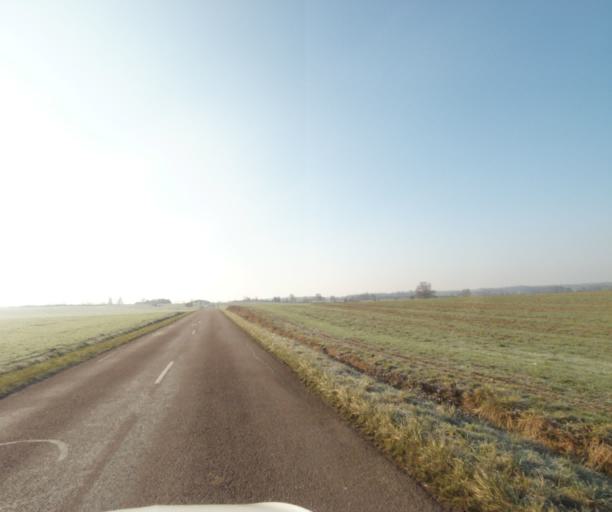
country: FR
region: Champagne-Ardenne
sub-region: Departement de la Haute-Marne
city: Montier-en-Der
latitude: 48.4181
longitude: 4.7435
